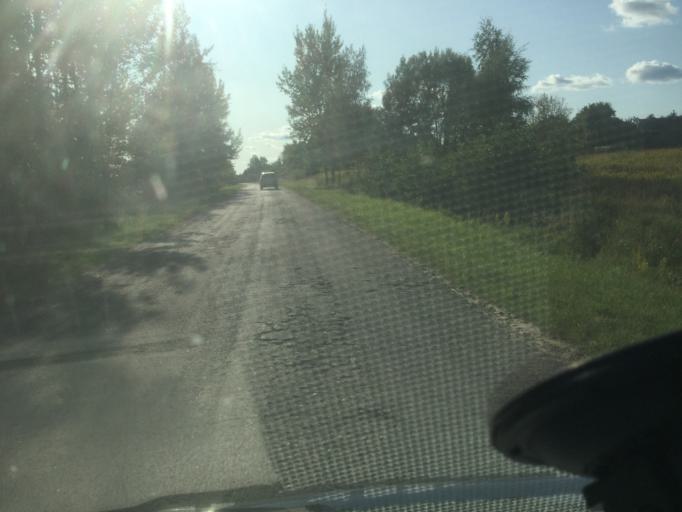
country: BY
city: Osveya
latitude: 56.0214
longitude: 28.2708
